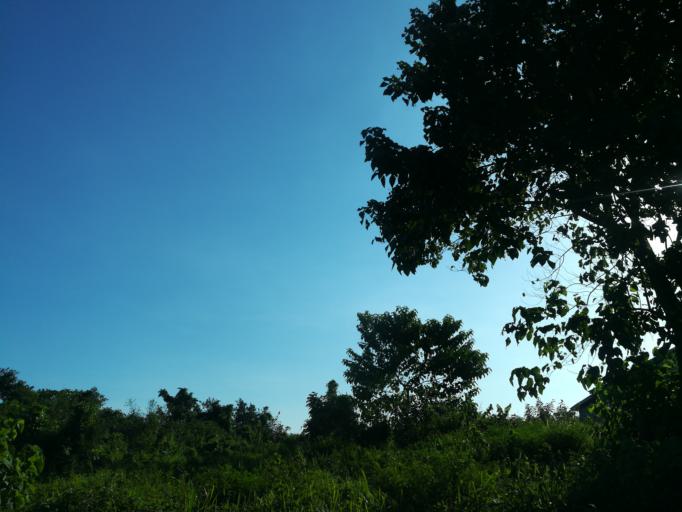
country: NG
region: Lagos
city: Ikorodu
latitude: 6.5691
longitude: 3.5332
